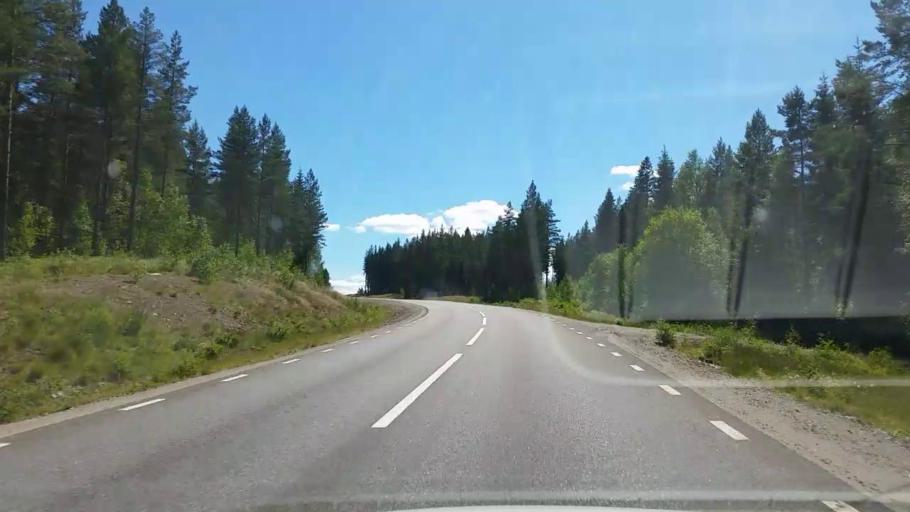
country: SE
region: Gaevleborg
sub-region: Ovanakers Kommun
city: Edsbyn
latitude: 61.0775
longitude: 15.7999
